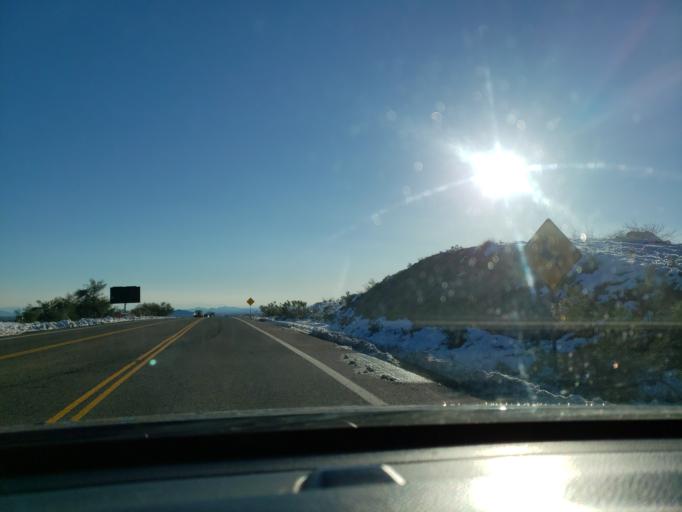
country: US
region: Arizona
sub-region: Maricopa County
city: Carefree
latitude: 33.8486
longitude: -111.8356
